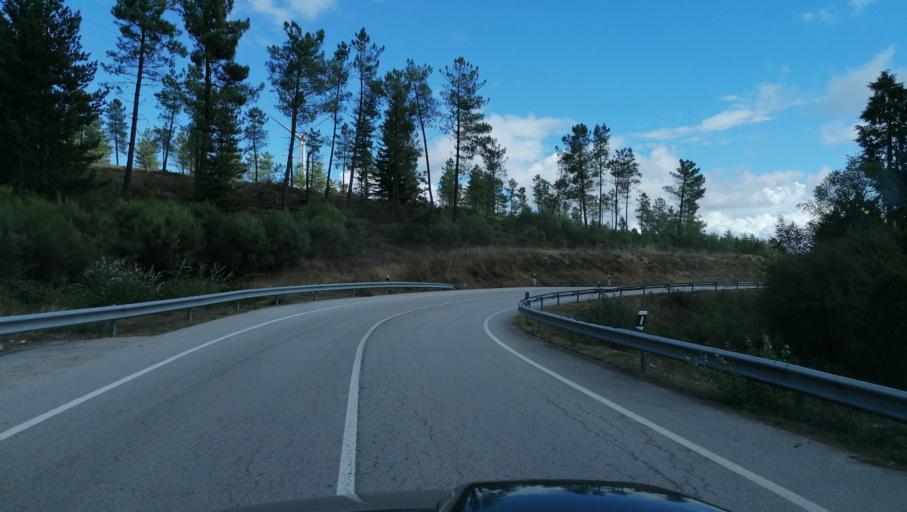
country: PT
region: Vila Real
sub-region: Vila Pouca de Aguiar
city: Vila Pouca de Aguiar
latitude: 41.5172
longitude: -7.5993
